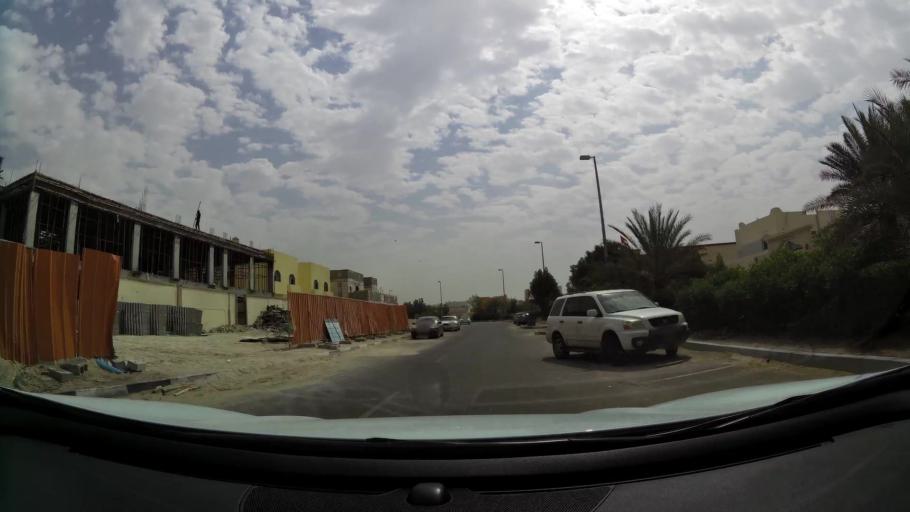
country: AE
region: Abu Dhabi
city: Abu Dhabi
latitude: 24.3133
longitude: 54.6345
